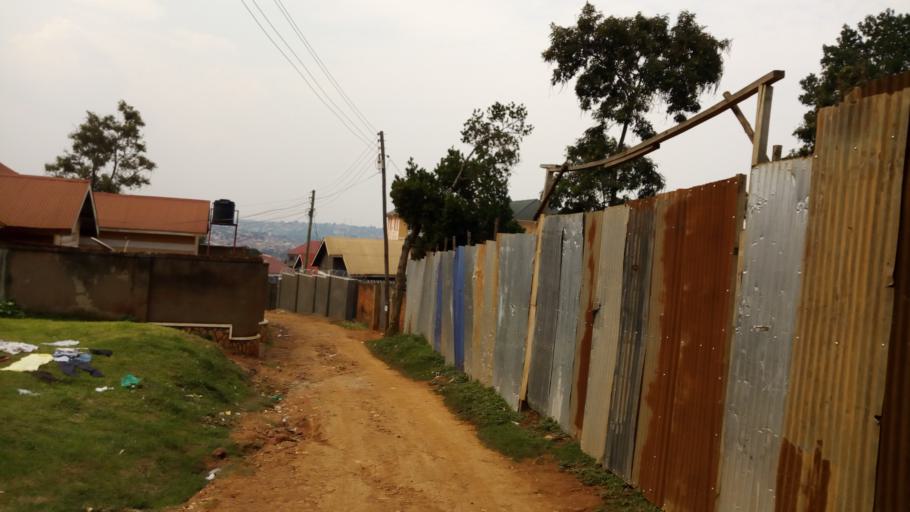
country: UG
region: Central Region
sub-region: Wakiso District
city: Kireka
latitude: 0.3191
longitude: 32.6437
